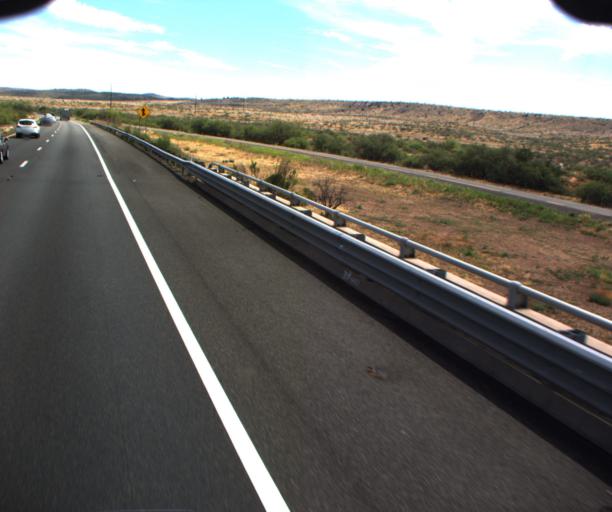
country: US
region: Arizona
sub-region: Yavapai County
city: Cordes Lakes
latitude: 34.4030
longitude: -112.0739
